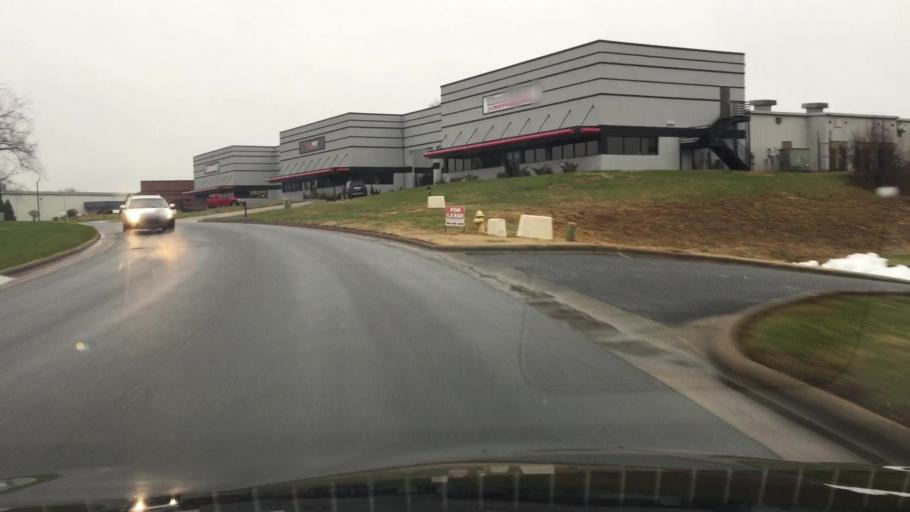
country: US
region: North Carolina
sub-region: Iredell County
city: Mooresville
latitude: 35.5873
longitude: -80.8616
